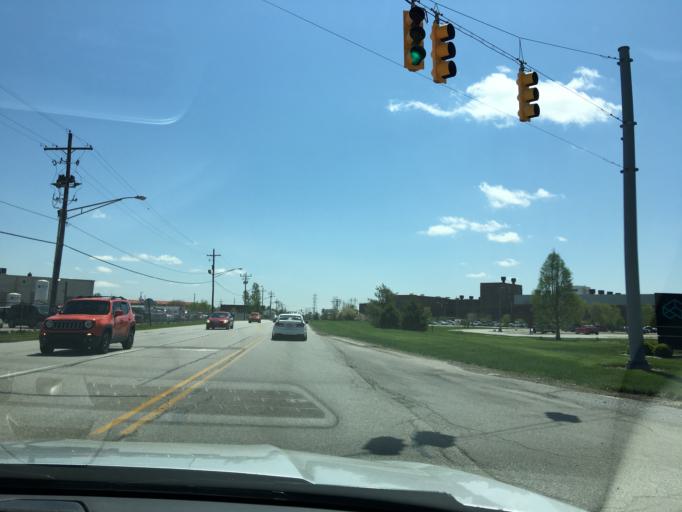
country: US
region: Indiana
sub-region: Tippecanoe County
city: Lafayette
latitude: 40.4040
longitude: -86.8623
